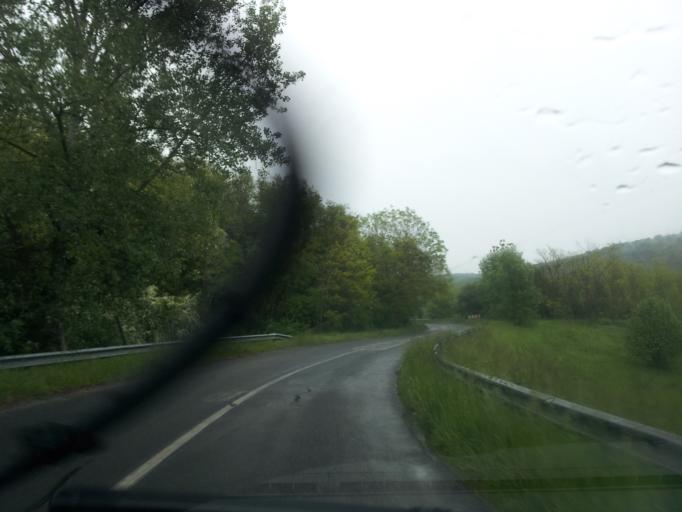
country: HU
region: Tolna
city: Bonyhad
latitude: 46.2670
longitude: 18.6176
